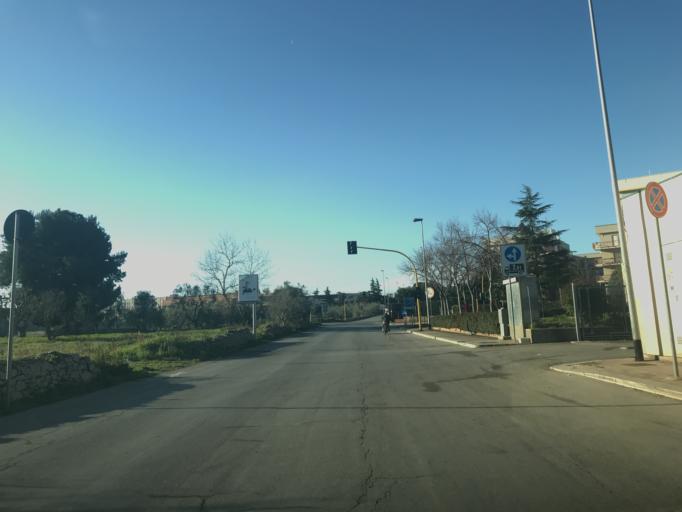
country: IT
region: Apulia
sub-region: Provincia di Bari
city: Corato
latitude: 41.1394
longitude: 16.4154
